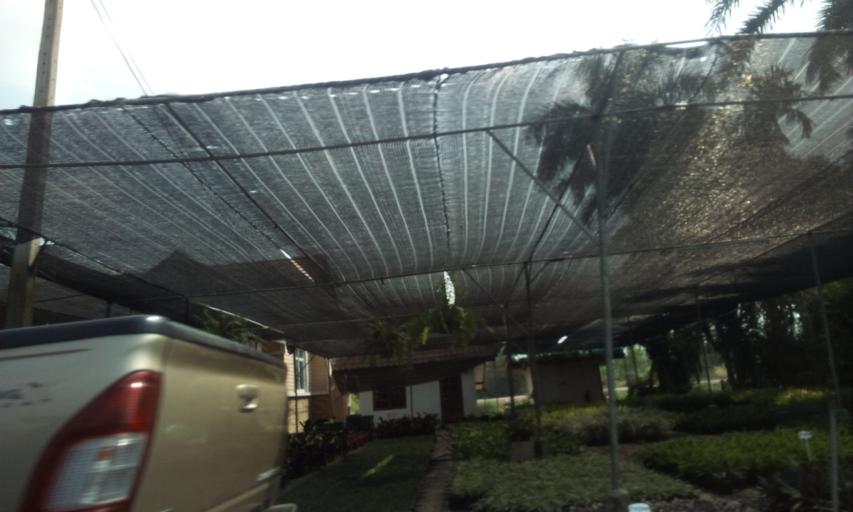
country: TH
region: Nakhon Nayok
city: Ongkharak
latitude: 14.1289
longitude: 100.9485
